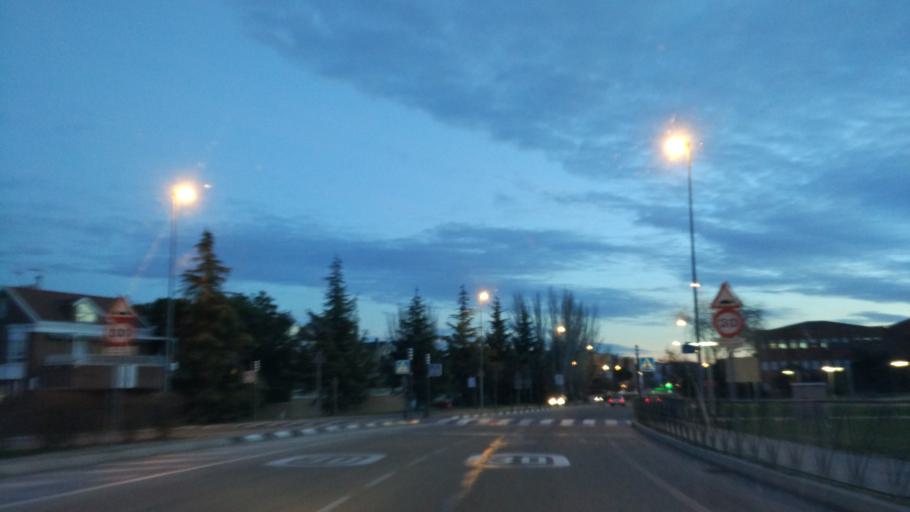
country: ES
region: Madrid
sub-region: Provincia de Madrid
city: Leganes
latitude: 40.3383
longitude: -3.7704
